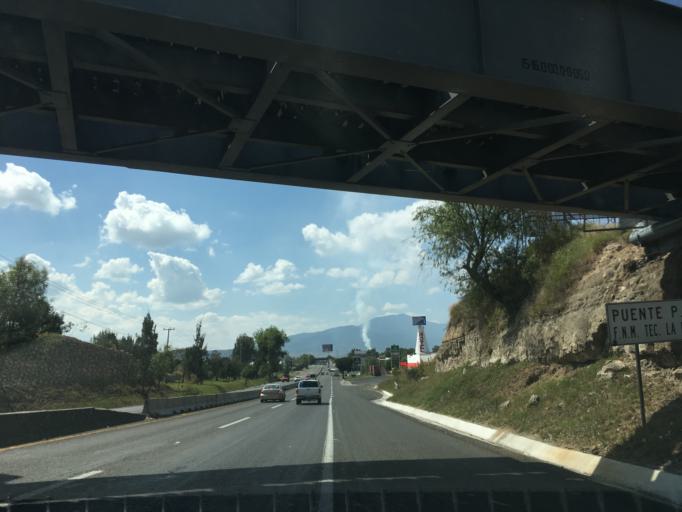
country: MX
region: Michoacan
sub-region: Morelia
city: Morelos
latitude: 19.6618
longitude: -101.2339
